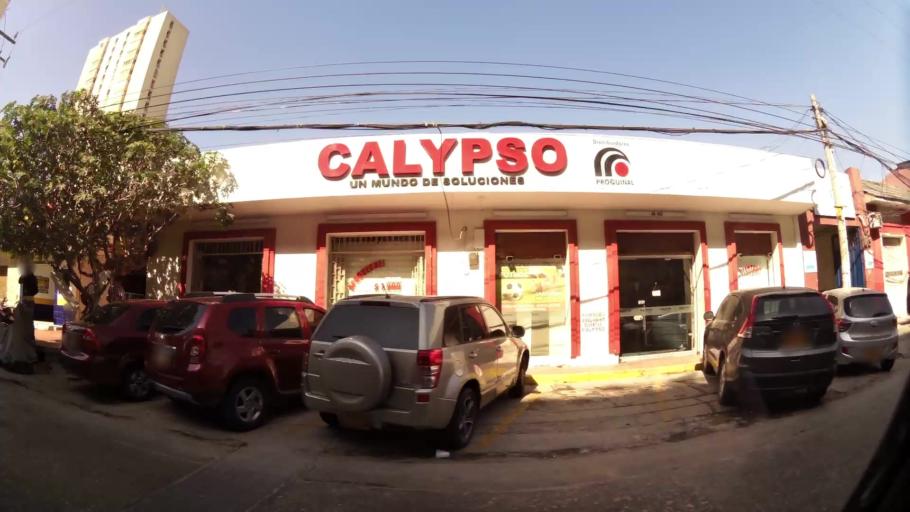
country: CO
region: Atlantico
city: Barranquilla
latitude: 10.9901
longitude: -74.7892
